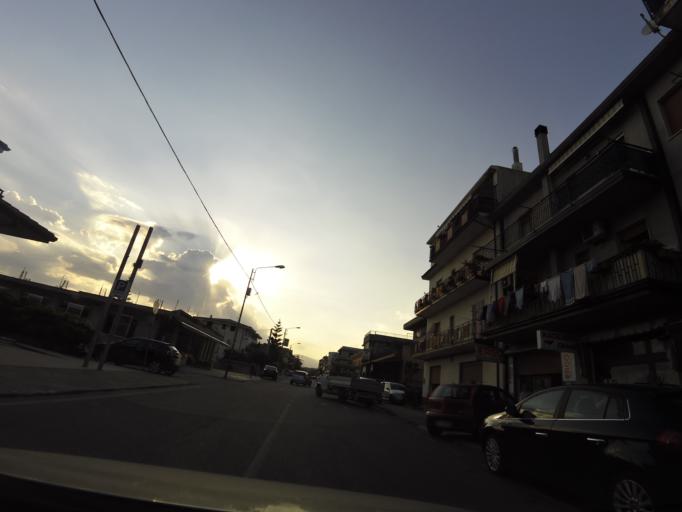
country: IT
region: Calabria
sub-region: Provincia di Reggio Calabria
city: Monasterace Marina
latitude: 38.4340
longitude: 16.5712
